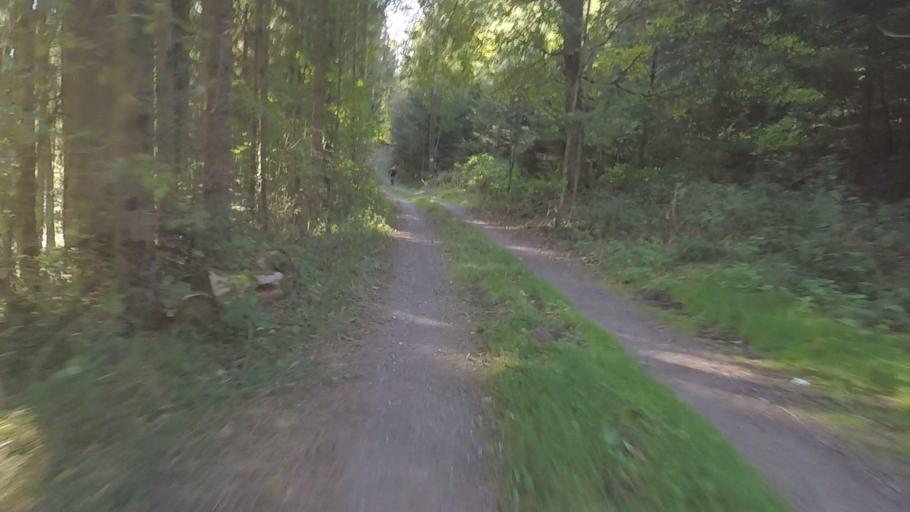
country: DE
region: Baden-Wuerttemberg
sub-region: Regierungsbezirk Stuttgart
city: Spiegelberg
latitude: 49.0345
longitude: 9.4643
